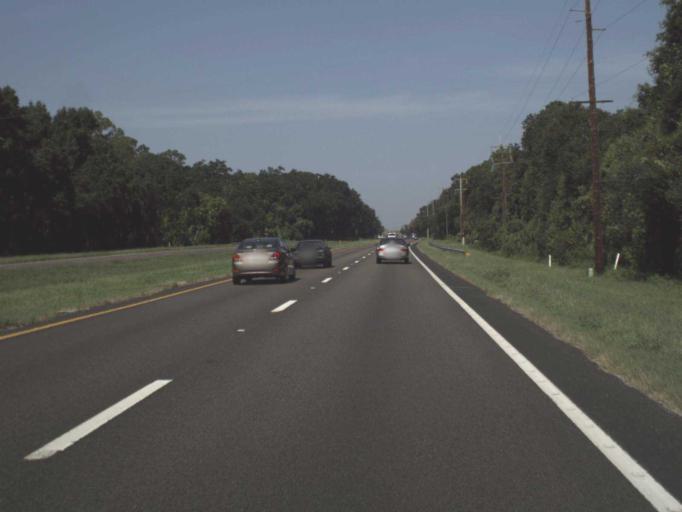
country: US
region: Florida
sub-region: Hillsborough County
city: Valrico
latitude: 27.9377
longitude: -82.1922
